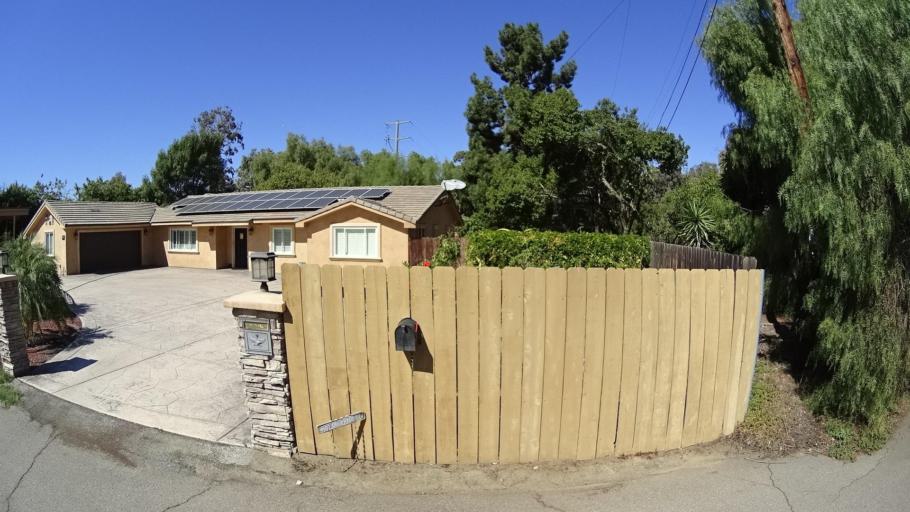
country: US
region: California
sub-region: San Diego County
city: Bonita
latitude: 32.6639
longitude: -117.0250
